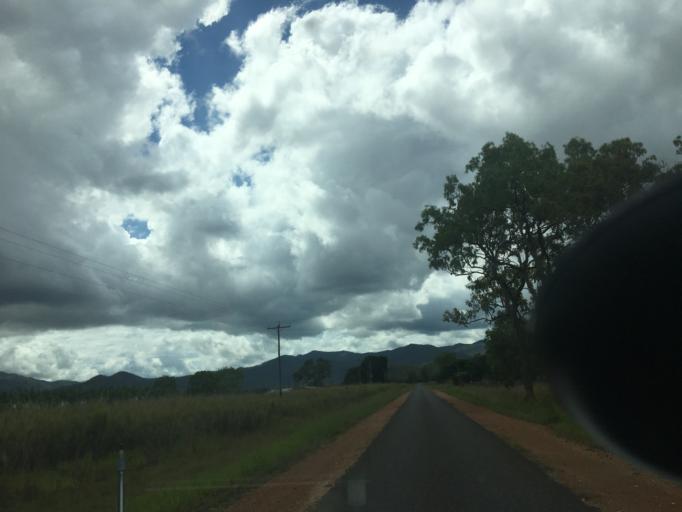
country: AU
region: Queensland
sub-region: Tablelands
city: Mareeba
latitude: -16.9953
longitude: 145.5223
